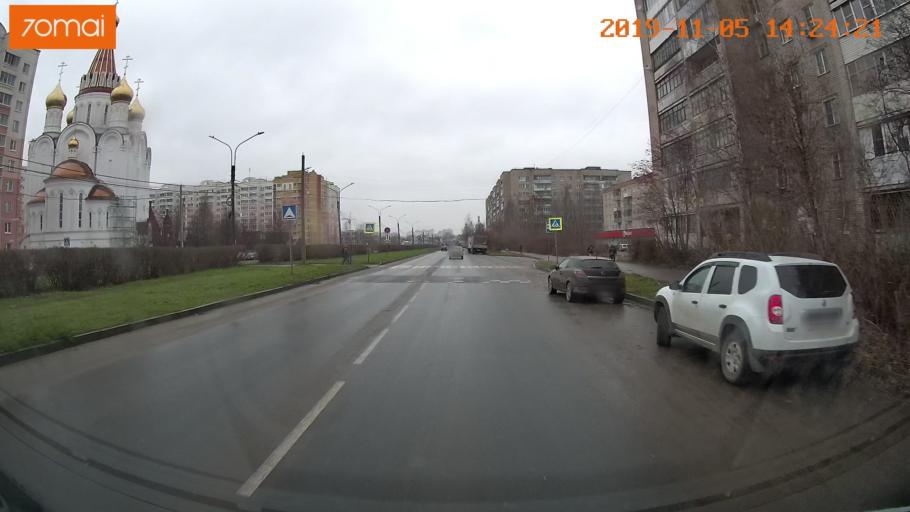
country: RU
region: Ivanovo
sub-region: Gorod Ivanovo
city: Ivanovo
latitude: 56.9683
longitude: 40.9977
